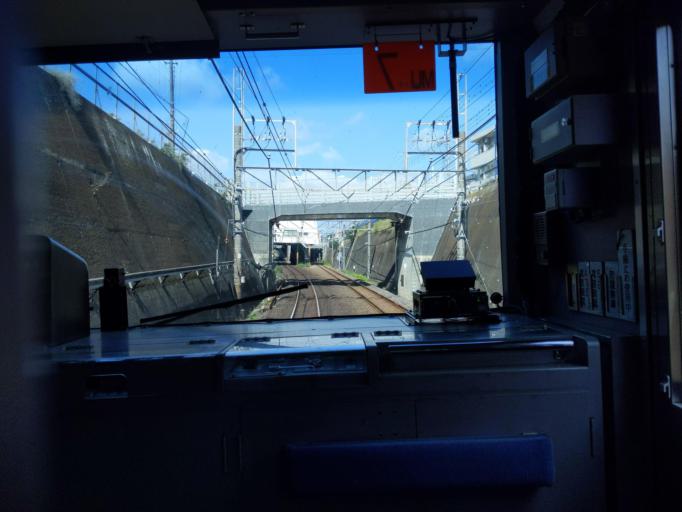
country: JP
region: Chiba
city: Funabashi
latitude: 35.7285
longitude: 139.9679
